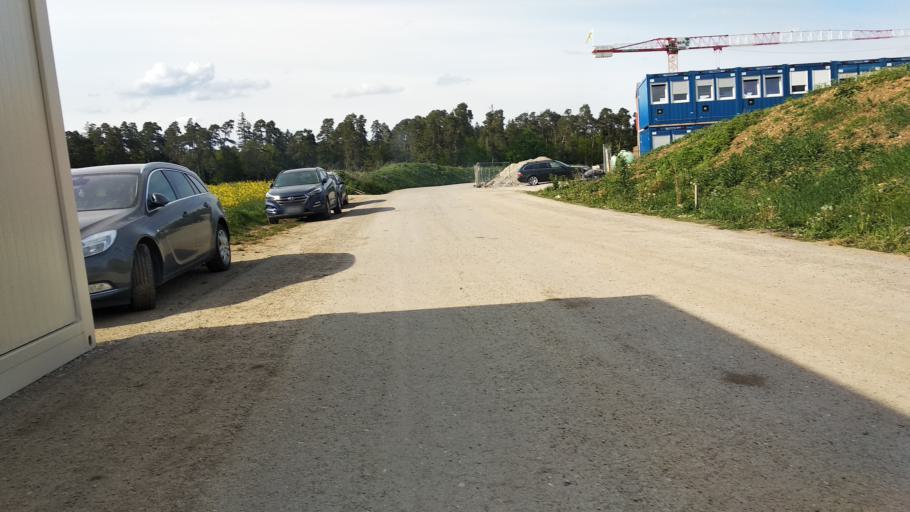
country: DE
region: Bavaria
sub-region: Upper Bavaria
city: Vaterstetten
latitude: 48.1137
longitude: 11.7657
